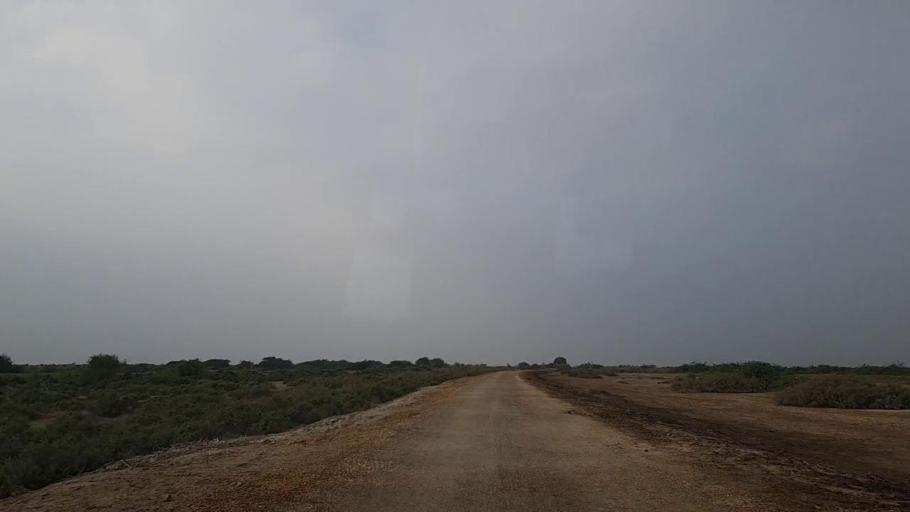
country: PK
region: Sindh
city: Mirpur Sakro
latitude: 24.6050
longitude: 67.5167
